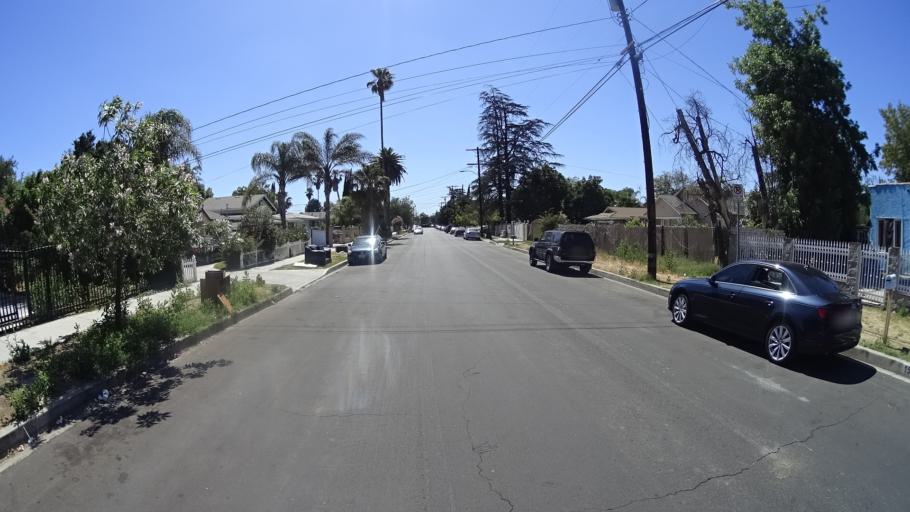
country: US
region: California
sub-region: Los Angeles County
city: Van Nuys
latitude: 34.1961
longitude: -118.4810
